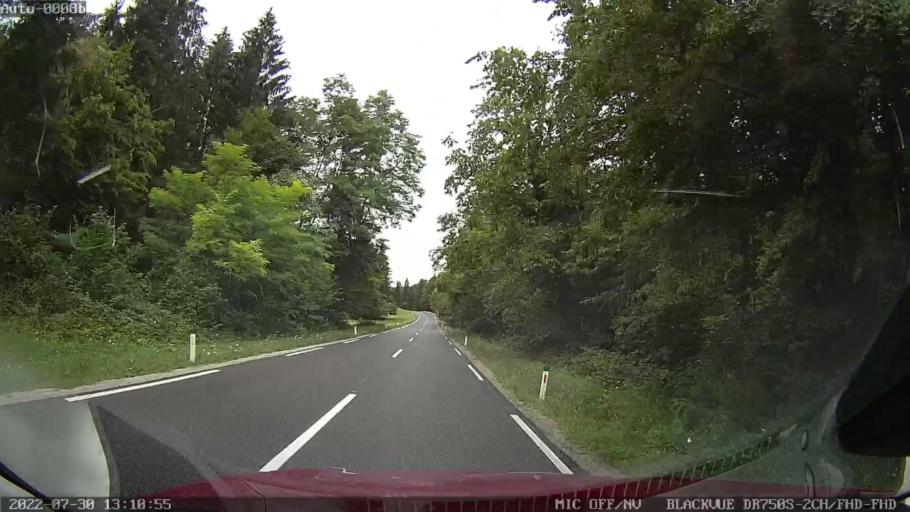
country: SI
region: Dolenjske Toplice
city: Dolenjske Toplice
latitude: 45.6987
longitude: 15.0832
